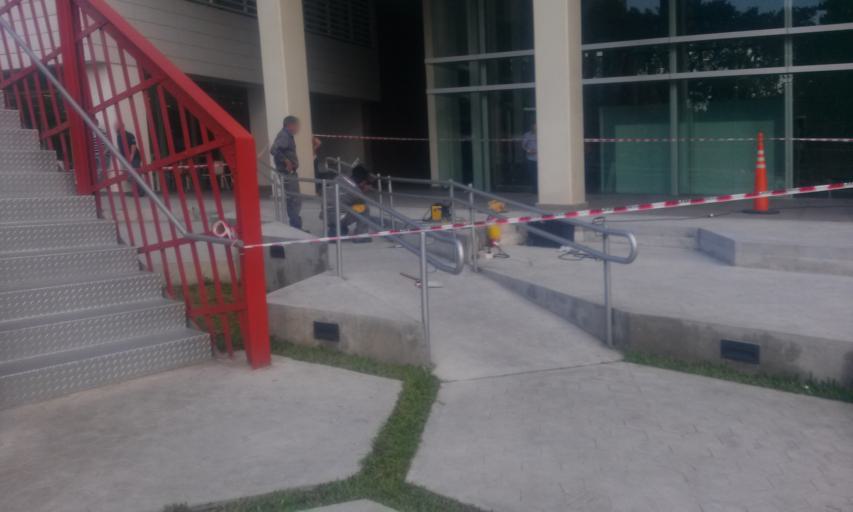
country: AR
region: Buenos Aires F.D.
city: Colegiales
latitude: -34.5825
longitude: -58.4294
